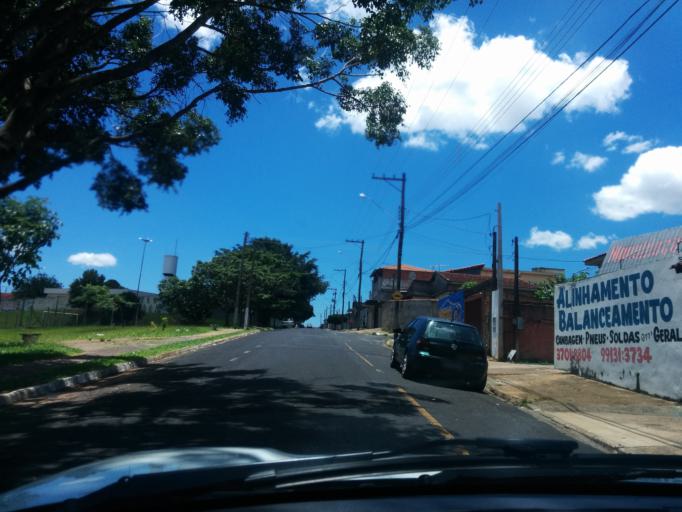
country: BR
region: Sao Paulo
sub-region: Franca
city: Franca
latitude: -20.5747
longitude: -47.3745
